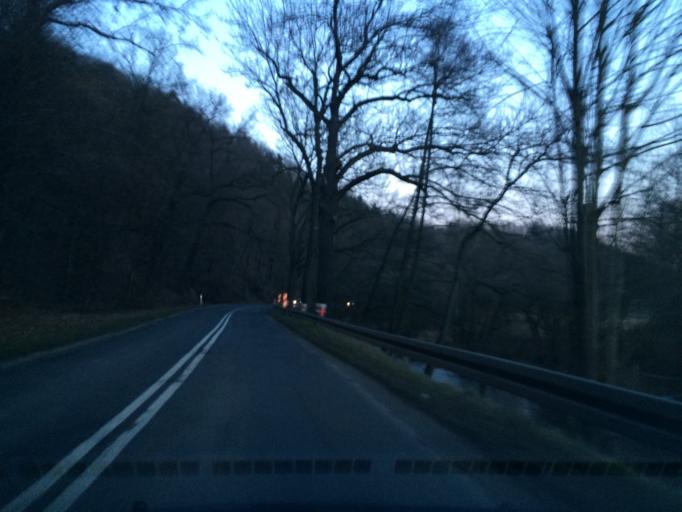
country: PL
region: Lower Silesian Voivodeship
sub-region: Powiat zlotoryjski
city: Zlotoryja
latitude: 51.1218
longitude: 15.8880
